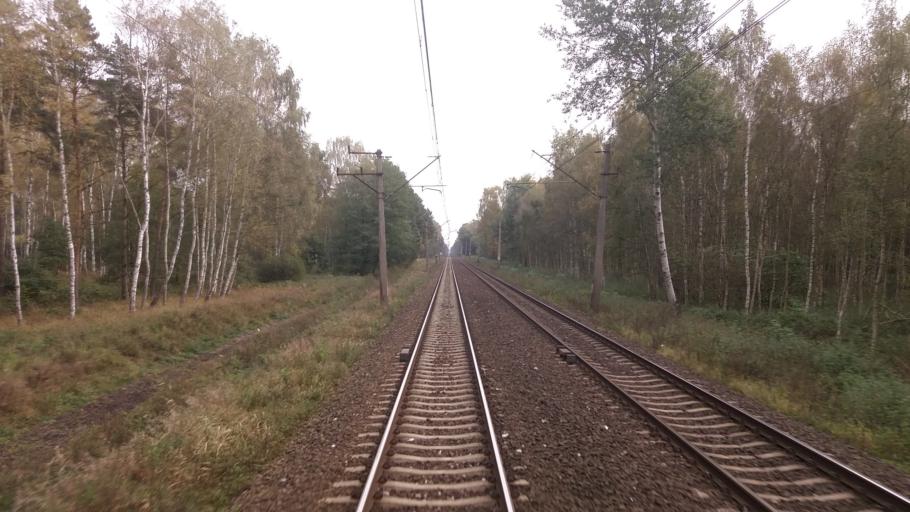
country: PL
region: West Pomeranian Voivodeship
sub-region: Powiat stargardzki
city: Kobylanka
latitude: 53.3787
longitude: 14.8059
